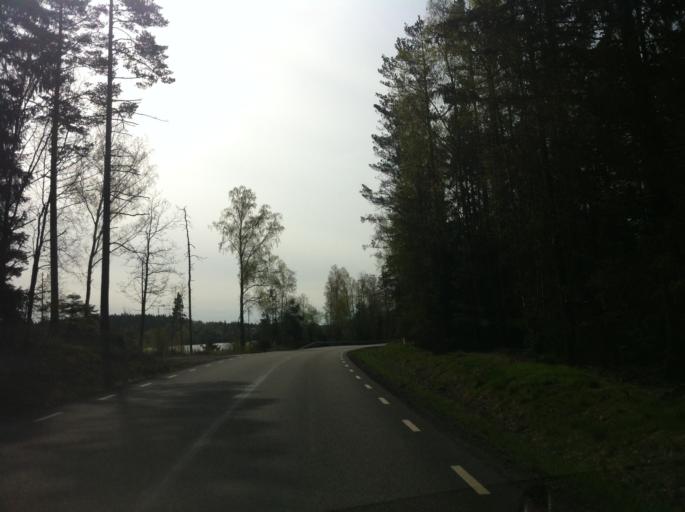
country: SE
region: Vaestra Goetaland
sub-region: Marks Kommun
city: Fritsla
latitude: 57.3706
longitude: 12.8617
